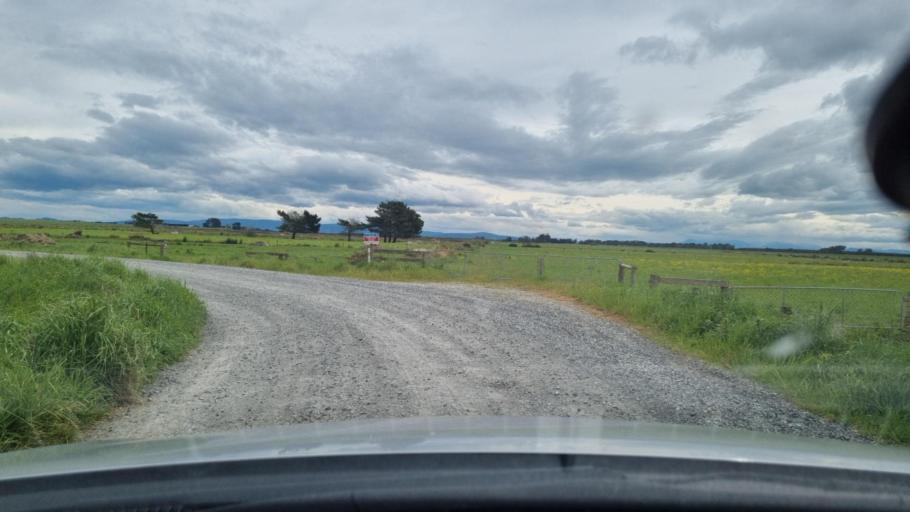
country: NZ
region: Southland
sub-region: Invercargill City
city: Invercargill
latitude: -46.4014
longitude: 168.2831
